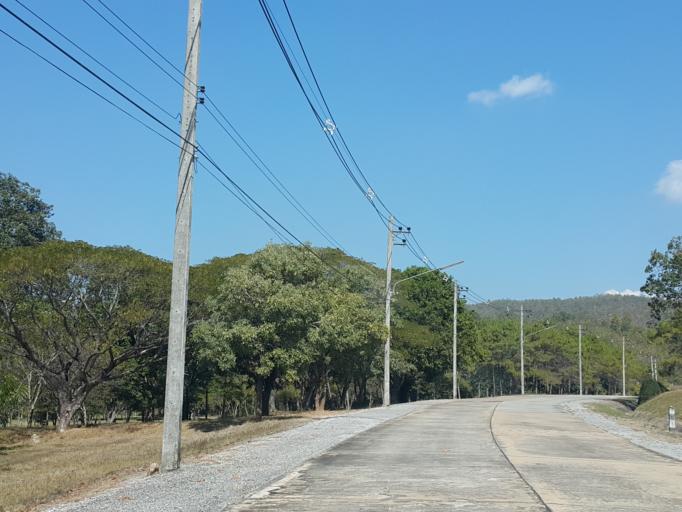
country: TH
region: Chiang Mai
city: Mae Taeng
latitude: 19.0232
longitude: 98.9935
